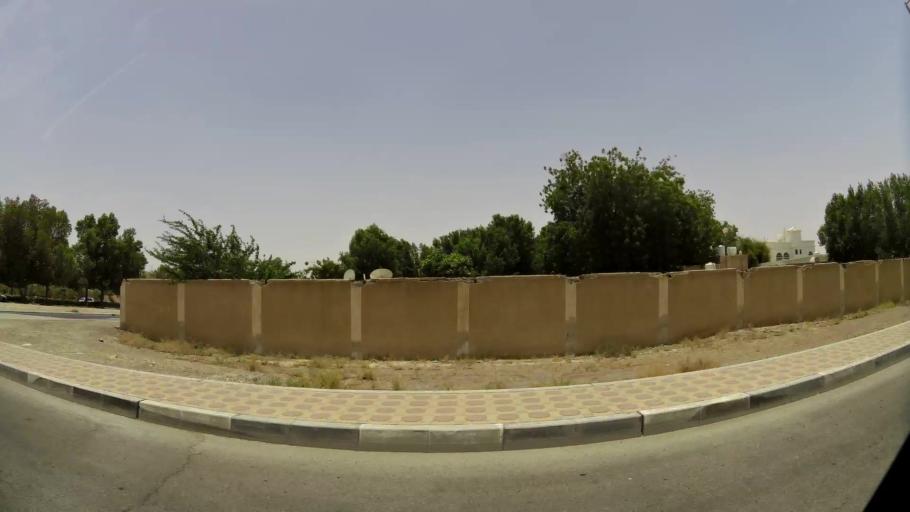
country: AE
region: Abu Dhabi
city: Al Ain
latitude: 24.2082
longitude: 55.7458
